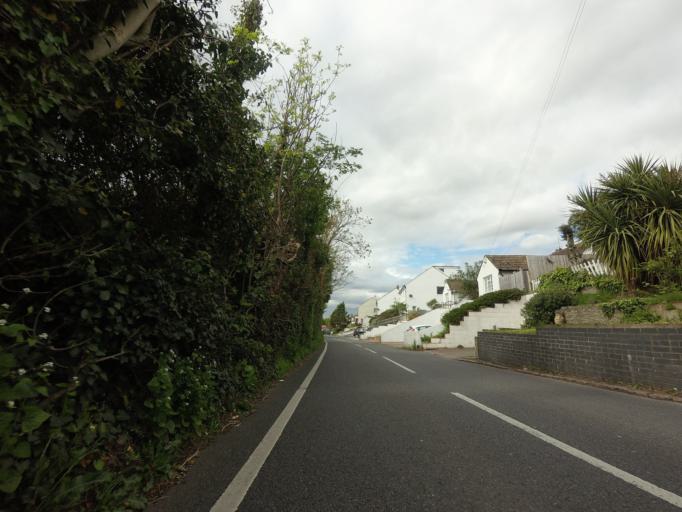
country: GB
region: England
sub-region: Greater London
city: Orpington
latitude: 51.3799
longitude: 0.1210
